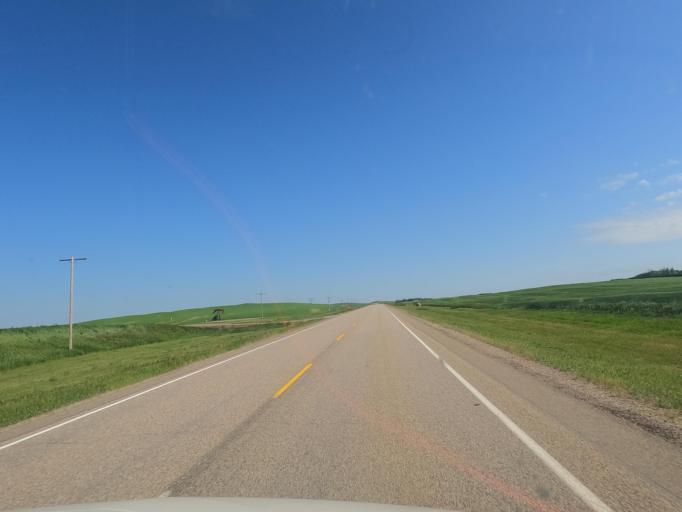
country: CA
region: Saskatchewan
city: Shaunavon
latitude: 49.9689
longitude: -108.4849
